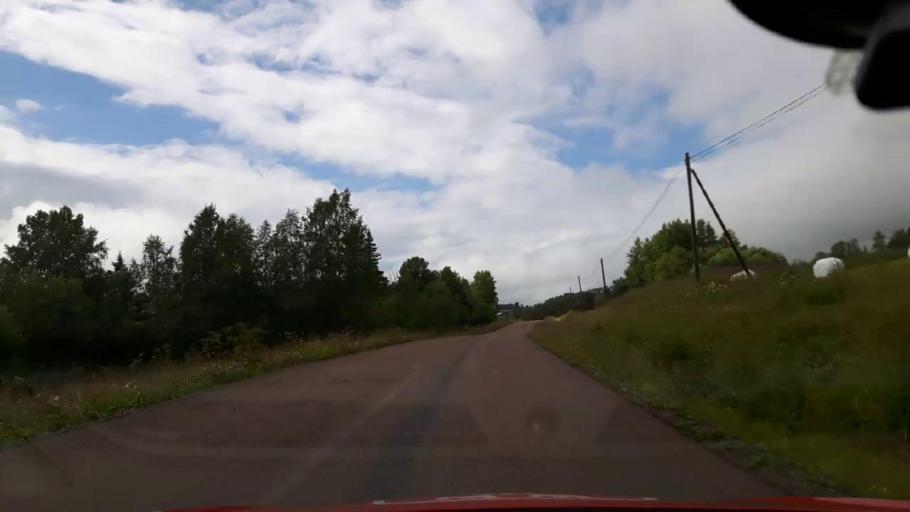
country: SE
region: Jaemtland
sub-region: Krokoms Kommun
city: Valla
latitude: 63.3843
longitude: 13.9769
